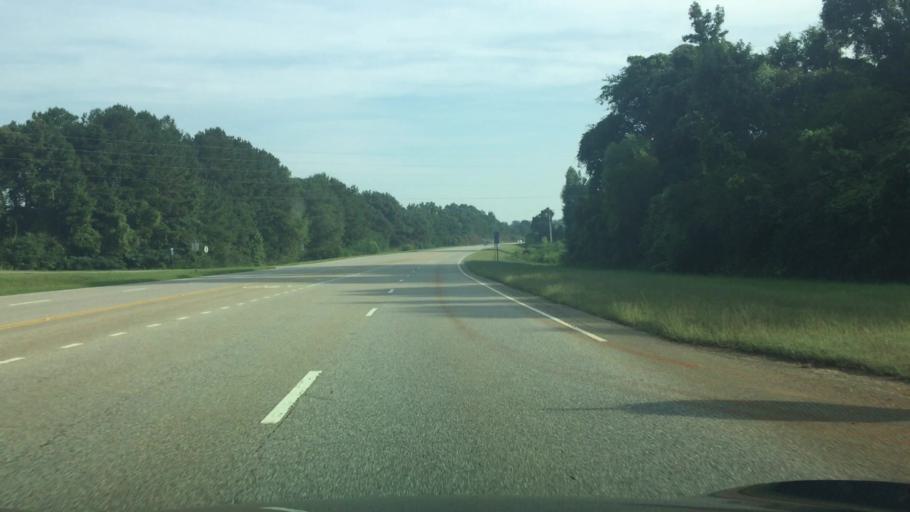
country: US
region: Alabama
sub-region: Covington County
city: Andalusia
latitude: 31.4222
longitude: -86.6111
